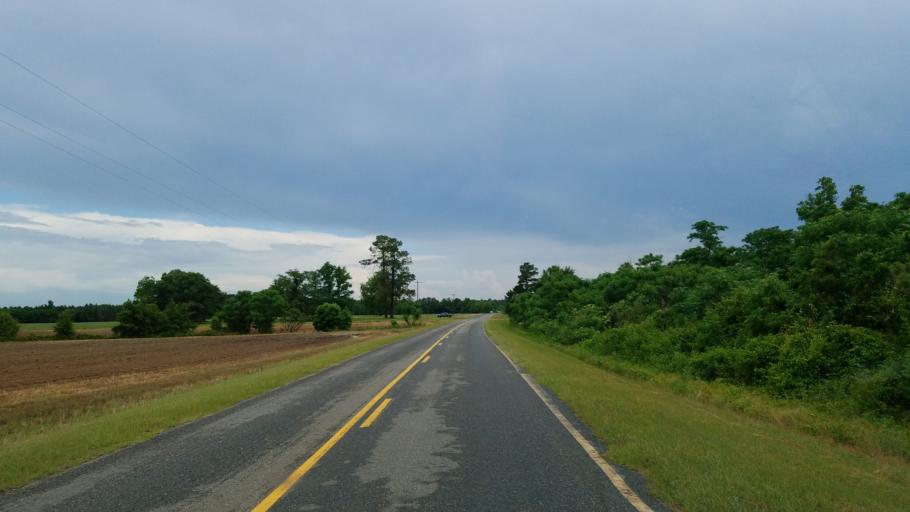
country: US
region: Georgia
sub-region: Dooly County
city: Unadilla
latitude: 32.2240
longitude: -83.7962
